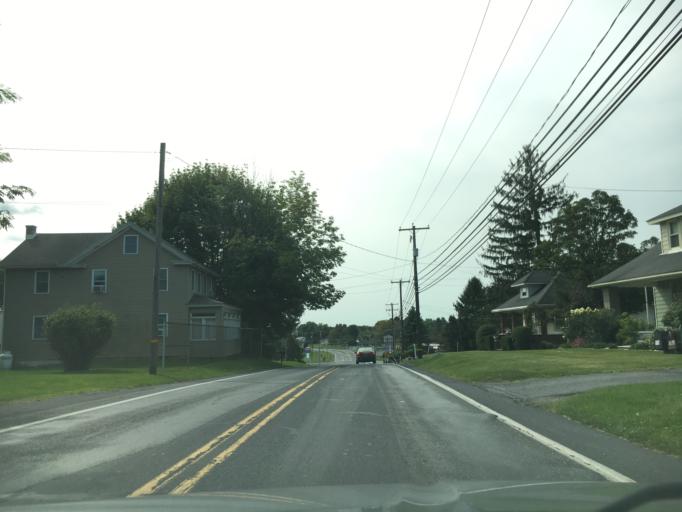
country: US
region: Pennsylvania
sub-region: Lehigh County
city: Schnecksville
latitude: 40.6797
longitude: -75.6136
